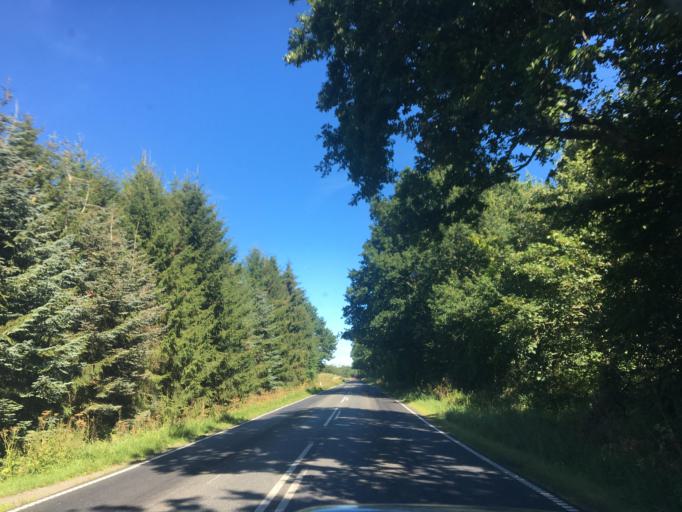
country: DK
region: South Denmark
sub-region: Assens Kommune
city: Arup
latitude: 55.4056
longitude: 10.0077
